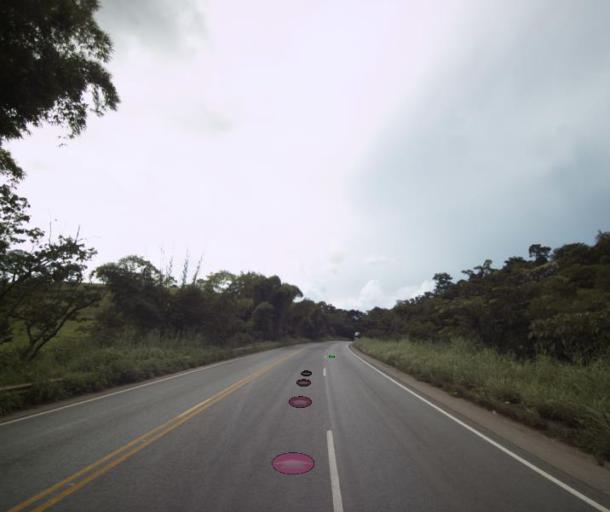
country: BR
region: Goias
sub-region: Rialma
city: Rialma
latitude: -15.2463
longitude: -49.5574
